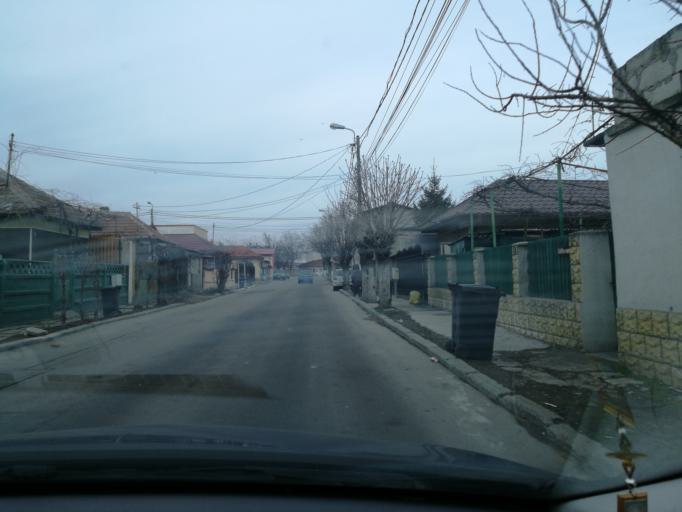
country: RO
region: Constanta
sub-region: Municipiul Constanta
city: Constanta
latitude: 44.1714
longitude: 28.6080
